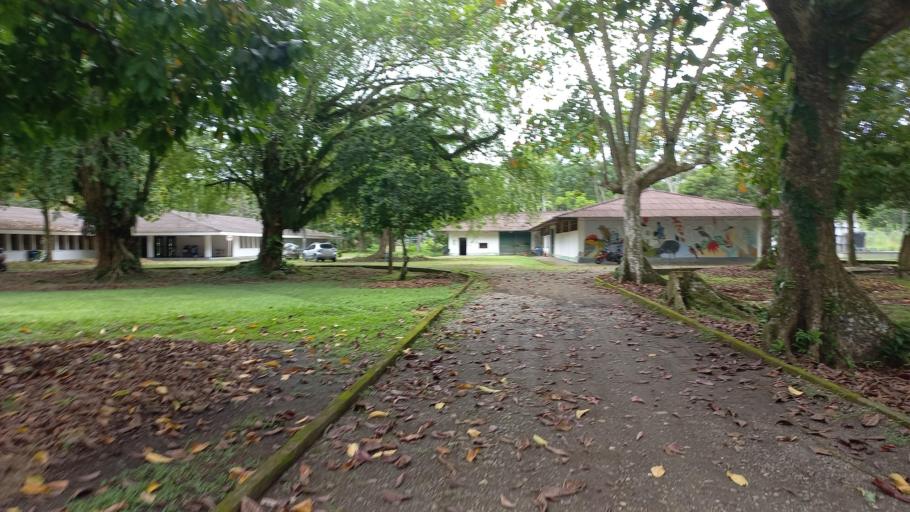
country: CO
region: Antioquia
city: Carepa
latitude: 7.7737
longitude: -76.6644
